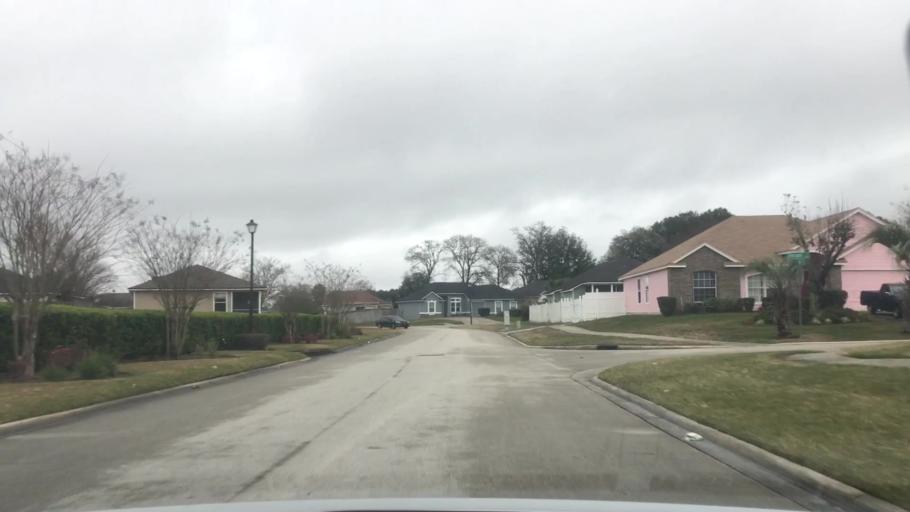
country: US
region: Florida
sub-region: Duval County
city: Jacksonville
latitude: 30.3598
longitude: -81.5752
